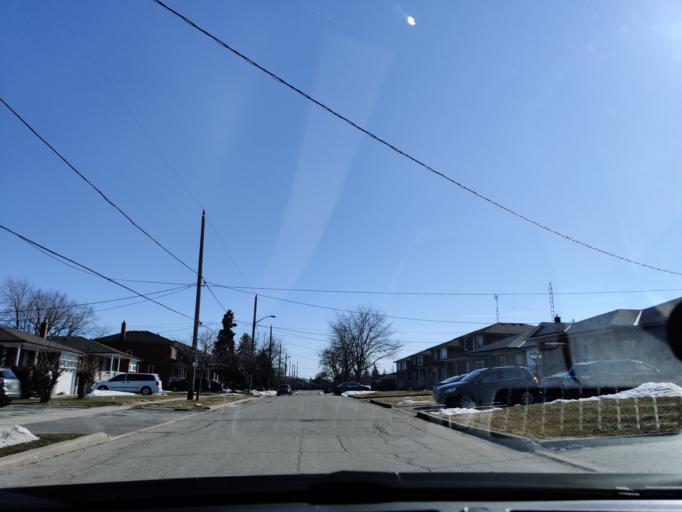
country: CA
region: Ontario
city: Toronto
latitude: 43.7213
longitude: -79.4770
